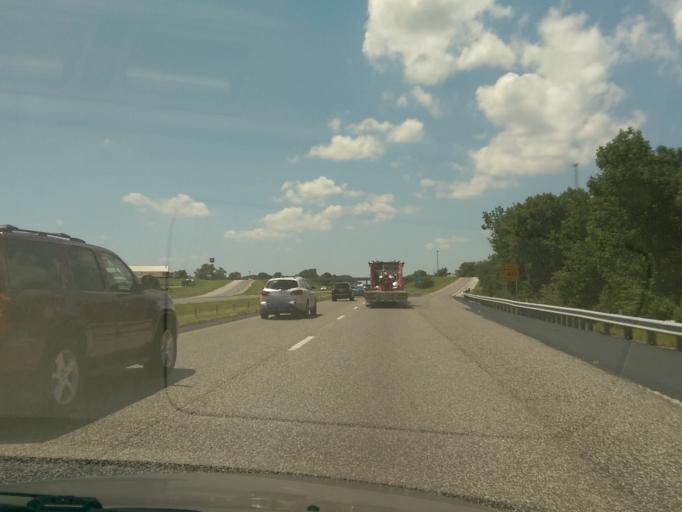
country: US
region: Missouri
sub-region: Cooper County
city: Boonville
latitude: 38.9399
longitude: -92.5928
